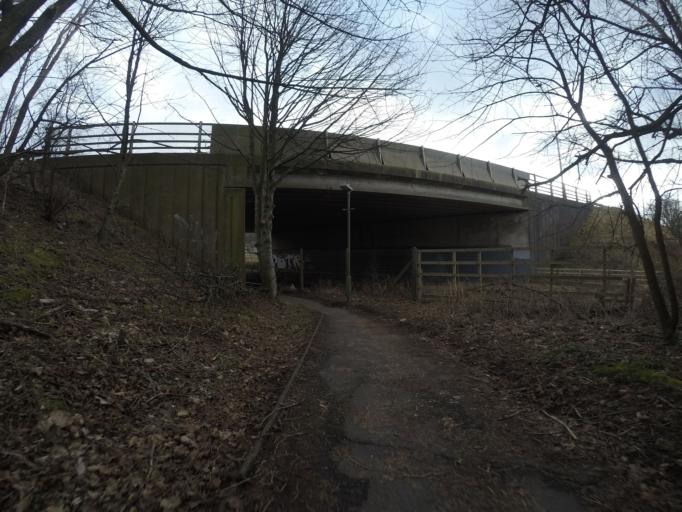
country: GB
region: Scotland
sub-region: South Ayrshire
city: Troon
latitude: 55.5695
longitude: -4.6388
